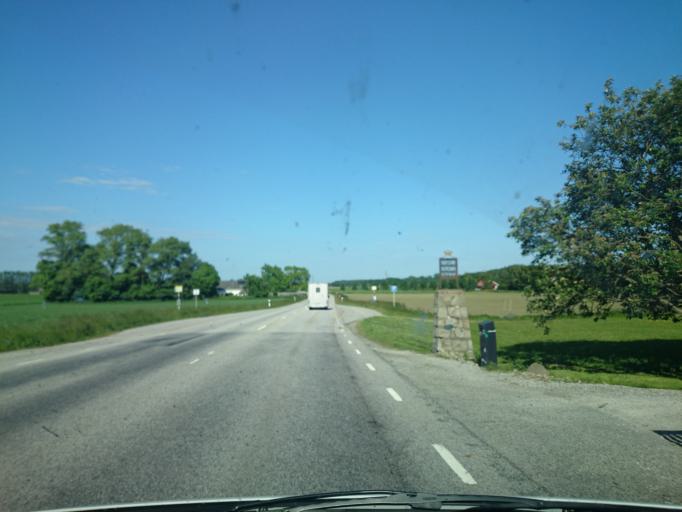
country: SE
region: Skane
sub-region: Lunds Kommun
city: Lund
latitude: 55.7066
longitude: 13.2602
